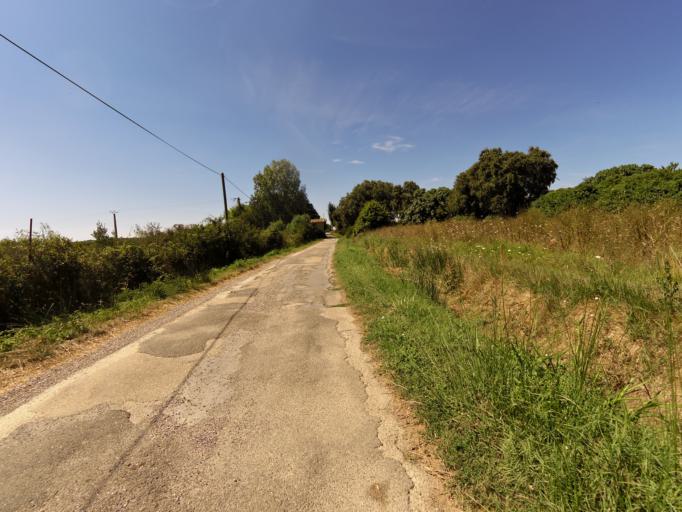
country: FR
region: Languedoc-Roussillon
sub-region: Departement du Gard
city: Aubais
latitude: 43.7517
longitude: 4.1362
